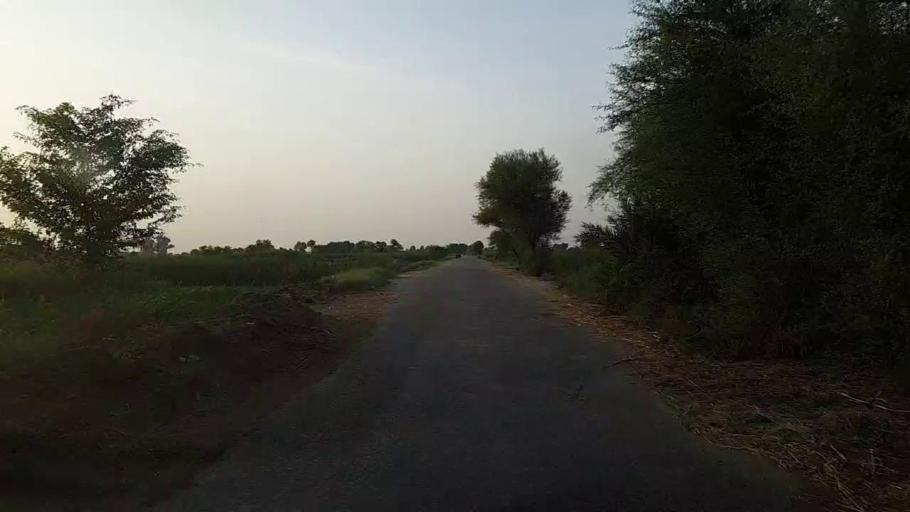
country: PK
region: Sindh
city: Ubauro
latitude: 28.2254
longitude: 69.8184
